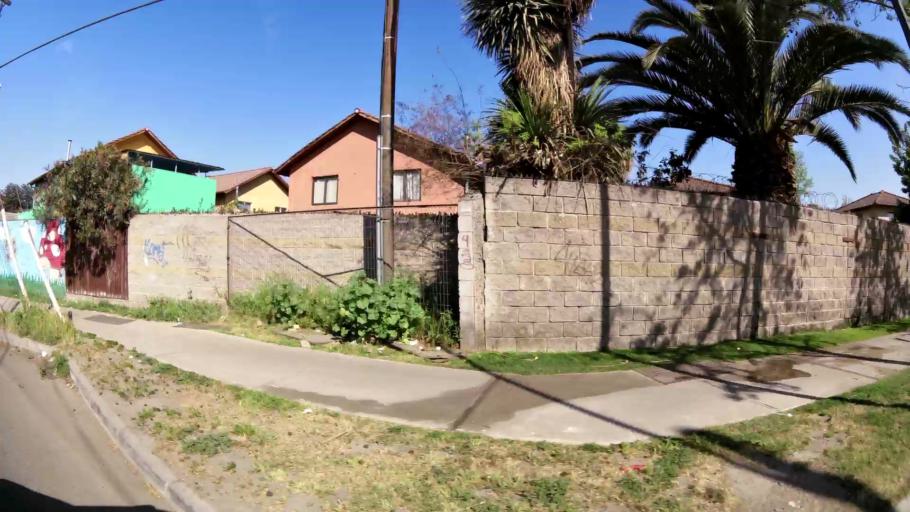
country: CL
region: Santiago Metropolitan
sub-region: Provincia de Chacabuco
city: Chicureo Abajo
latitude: -33.3598
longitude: -70.6760
